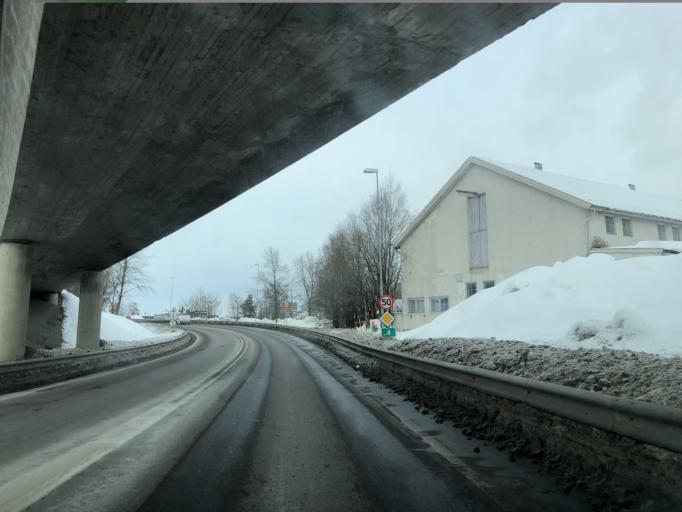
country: NO
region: Oppland
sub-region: Gjovik
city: Gjovik
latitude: 60.7929
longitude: 10.6968
